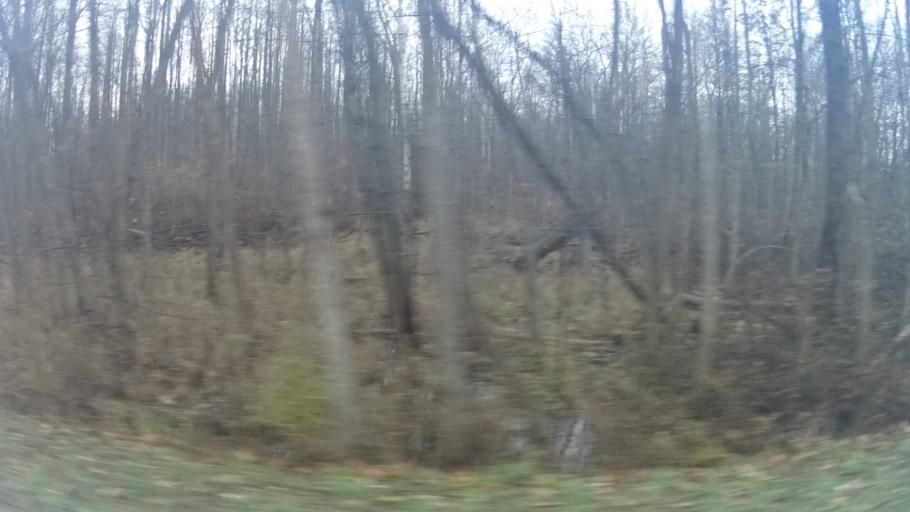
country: US
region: Ohio
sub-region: Lorain County
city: Lagrange
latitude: 41.2855
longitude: -82.1371
